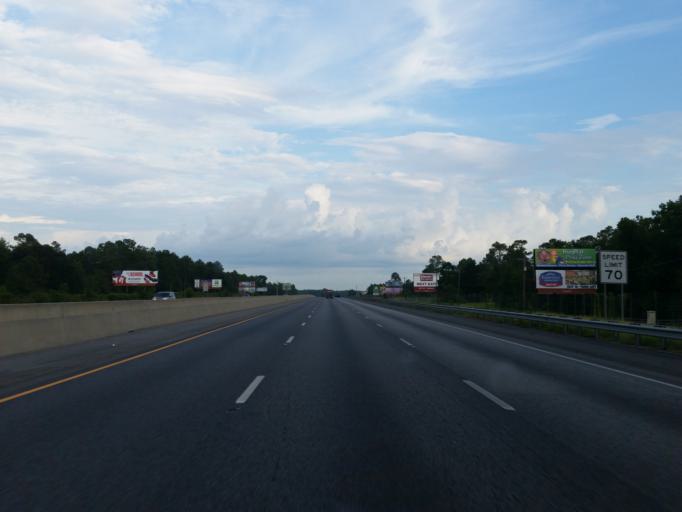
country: US
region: Georgia
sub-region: Lowndes County
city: Remerton
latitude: 30.8844
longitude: -83.3488
